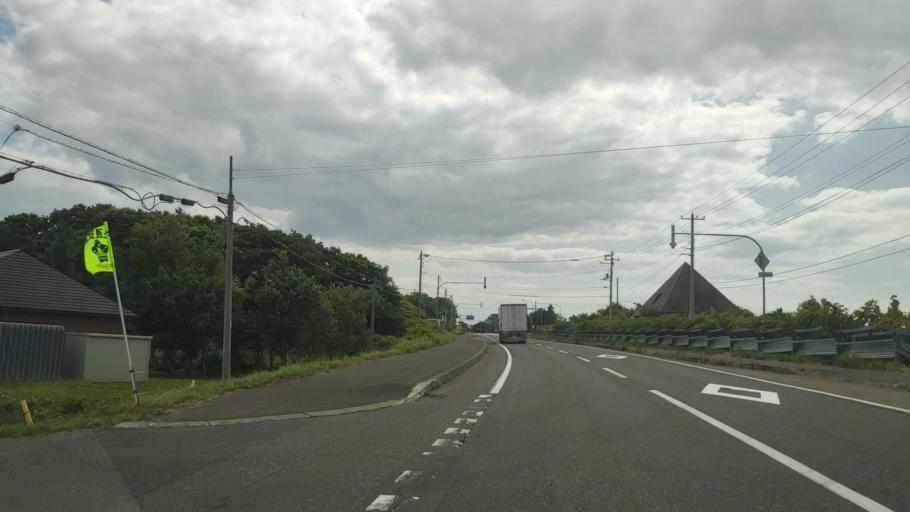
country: JP
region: Hokkaido
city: Rumoi
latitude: 44.5652
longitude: 141.7861
